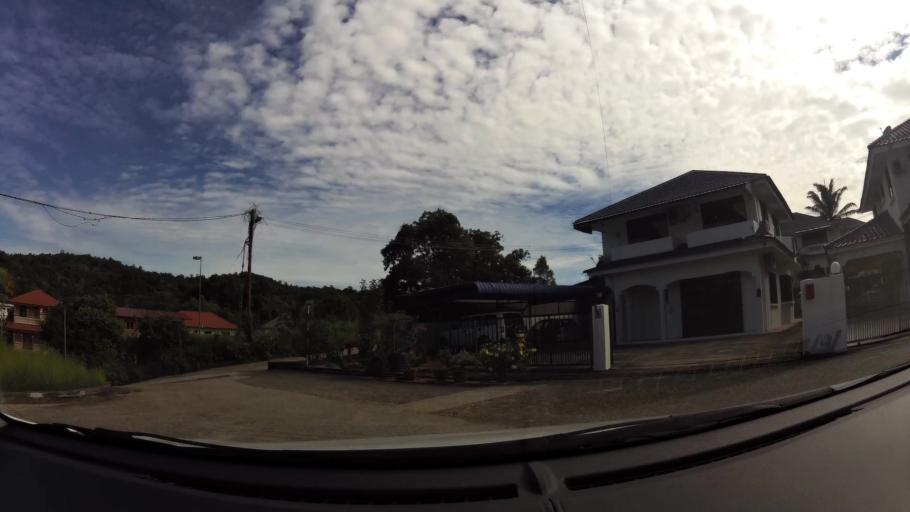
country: BN
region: Brunei and Muara
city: Bandar Seri Begawan
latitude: 4.9089
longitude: 114.9824
